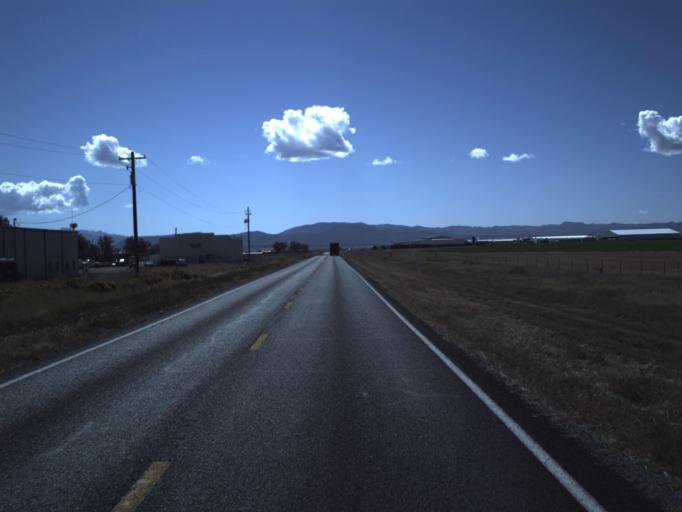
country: US
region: Utah
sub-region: Washington County
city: Enterprise
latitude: 37.6865
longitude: -113.6565
